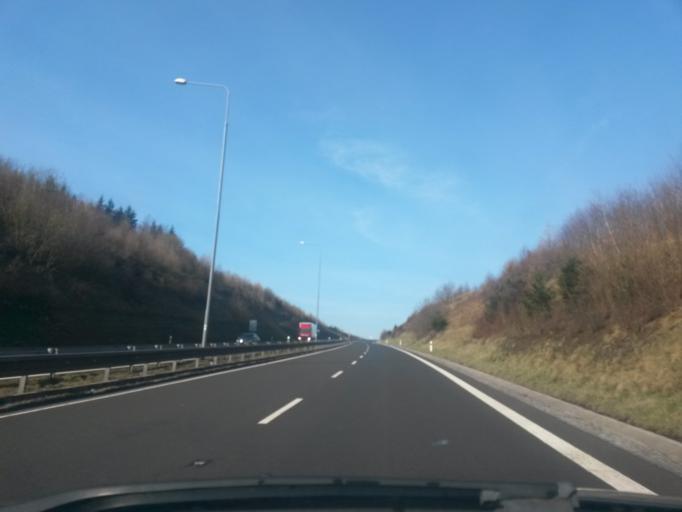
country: CZ
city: Krasna Lipa
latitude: 50.4770
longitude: 13.3353
